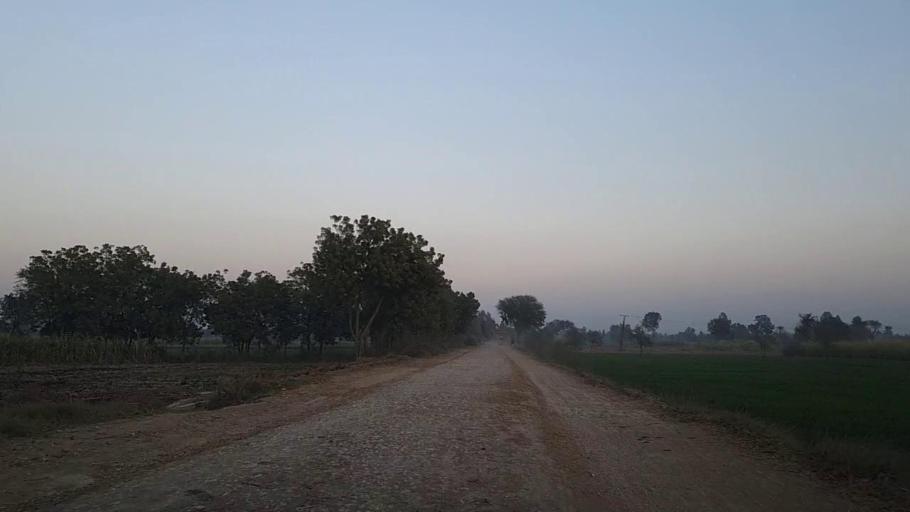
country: PK
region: Sindh
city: Naushahro Firoz
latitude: 26.8001
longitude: 68.0267
